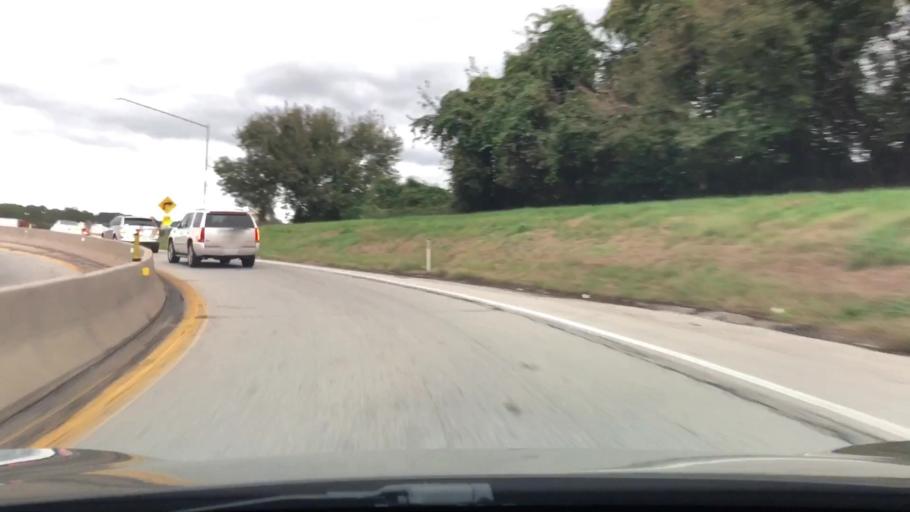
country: US
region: Pennsylvania
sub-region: Bucks County
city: Trevose
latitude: 40.1328
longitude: -74.9644
